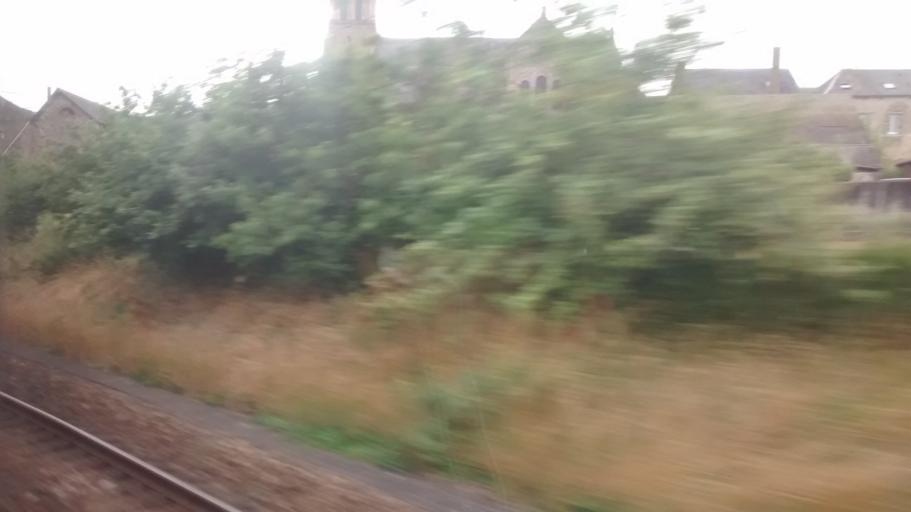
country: FR
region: Pays de la Loire
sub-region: Departement de la Mayenne
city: Louverne
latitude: 48.1223
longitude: -0.6755
